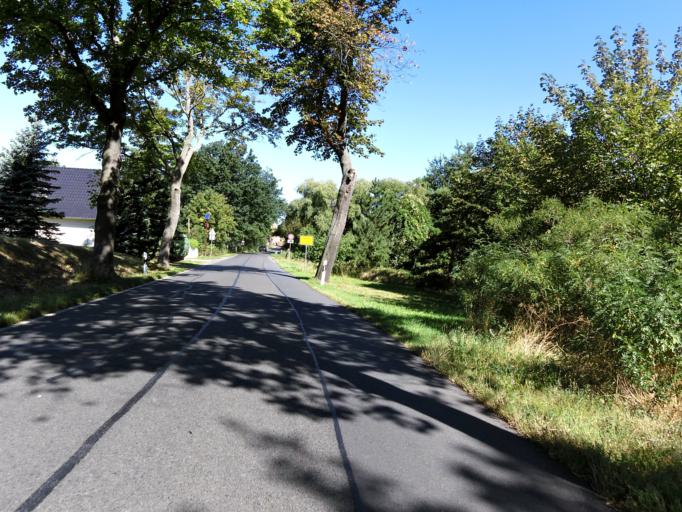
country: DE
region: Saxony-Anhalt
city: Pretzsch
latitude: 51.6842
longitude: 12.8271
